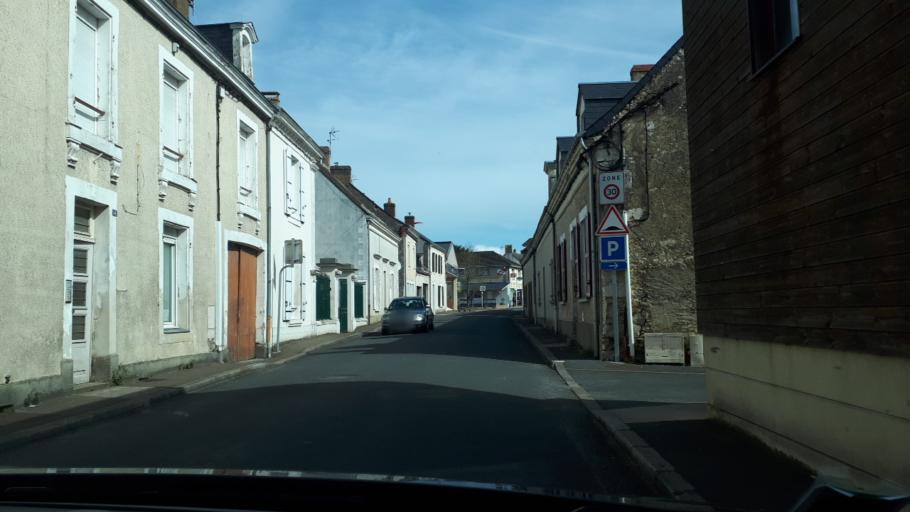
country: FR
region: Pays de la Loire
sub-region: Departement de la Sarthe
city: Yvre-le-Polin
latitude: 47.8189
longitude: 0.1530
